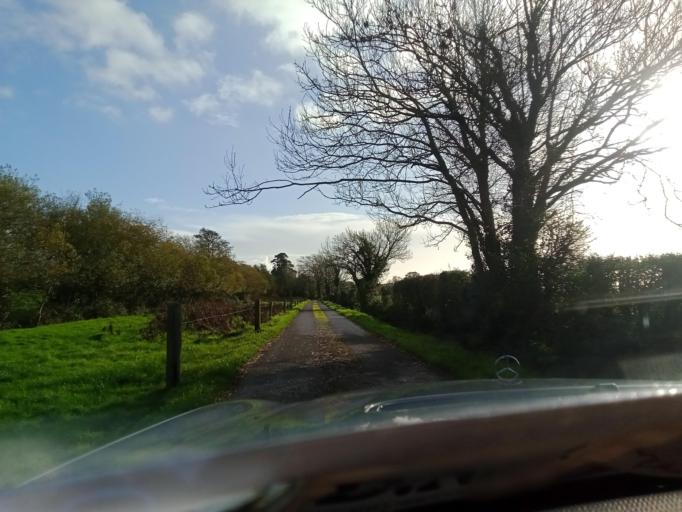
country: IE
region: Leinster
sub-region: Kilkenny
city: Mooncoin
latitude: 52.3293
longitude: -7.2776
